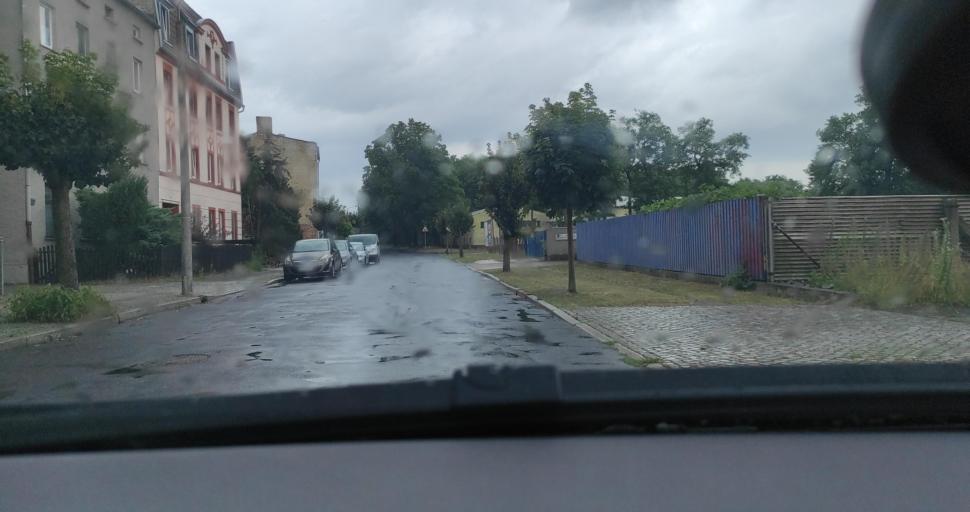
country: DE
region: Brandenburg
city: Forst
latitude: 51.7316
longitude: 14.6380
